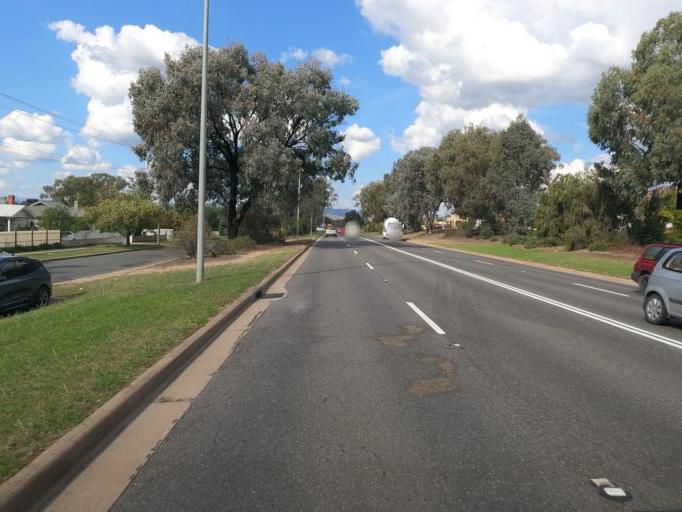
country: AU
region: New South Wales
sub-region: Albury Municipality
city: East Albury
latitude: -36.0760
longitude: 146.9334
